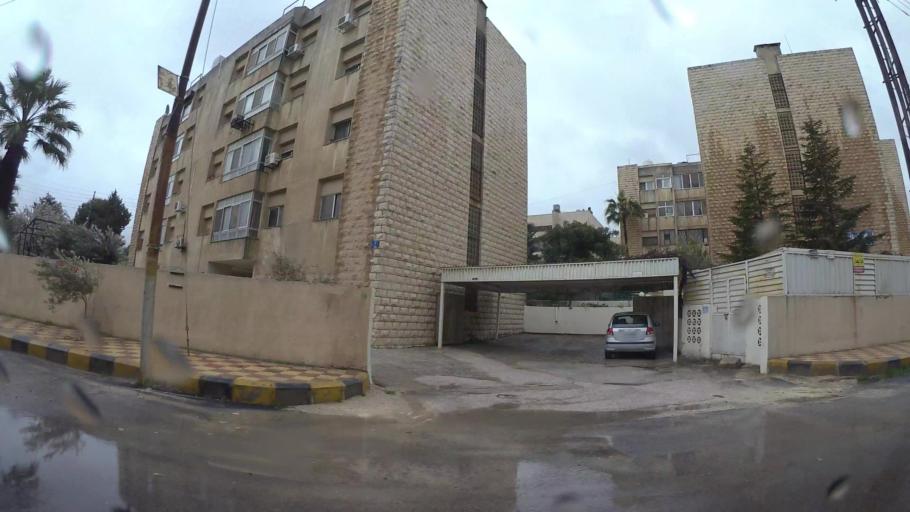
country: JO
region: Amman
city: Al Jubayhah
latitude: 32.0275
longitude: 35.8773
